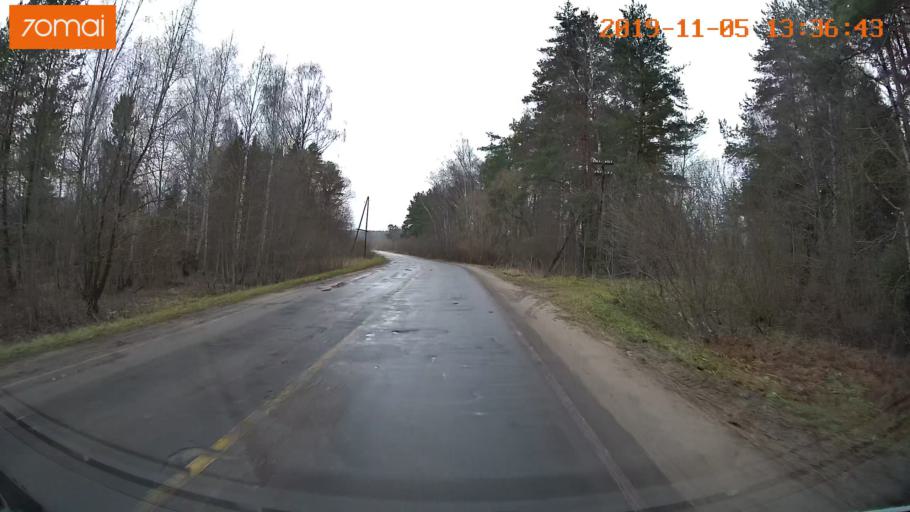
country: RU
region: Ivanovo
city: Shuya
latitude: 56.9167
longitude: 41.3823
